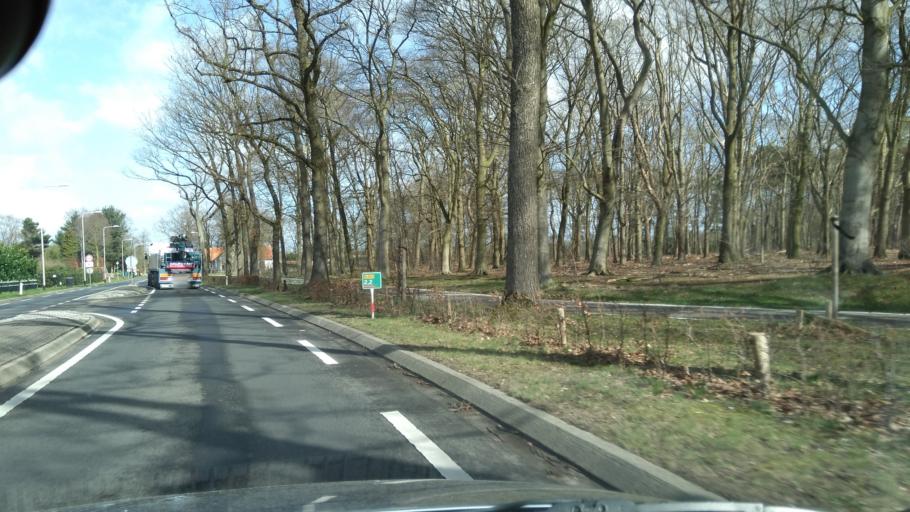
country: NL
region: North Brabant
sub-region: Gemeente Baarle-Nassau
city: Baarle-Nassau
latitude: 51.4037
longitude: 4.9368
